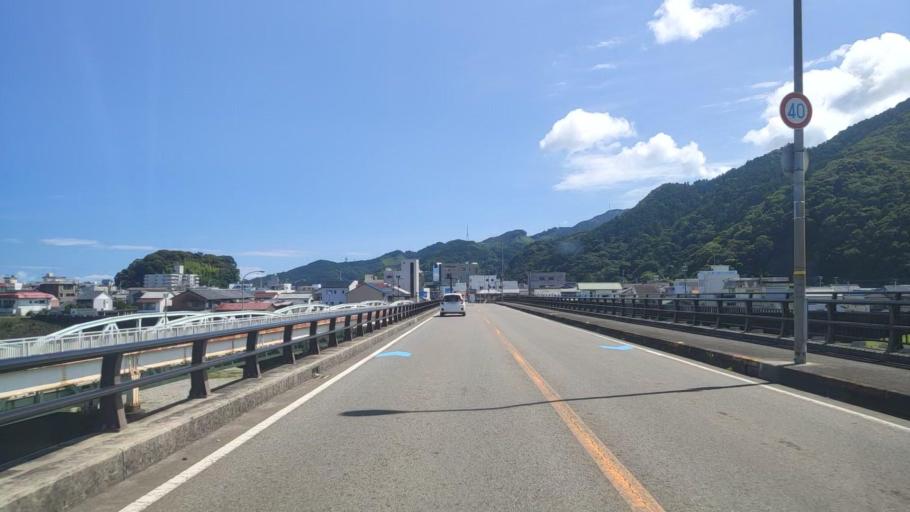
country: JP
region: Wakayama
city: Shingu
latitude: 33.7327
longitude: 135.9875
